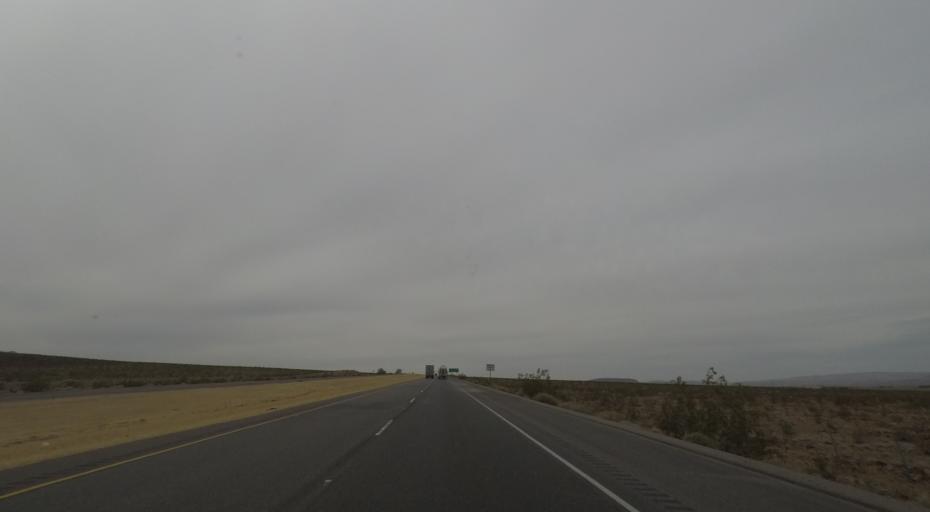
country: US
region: California
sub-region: San Bernardino County
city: Barstow
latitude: 34.8391
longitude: -116.7854
